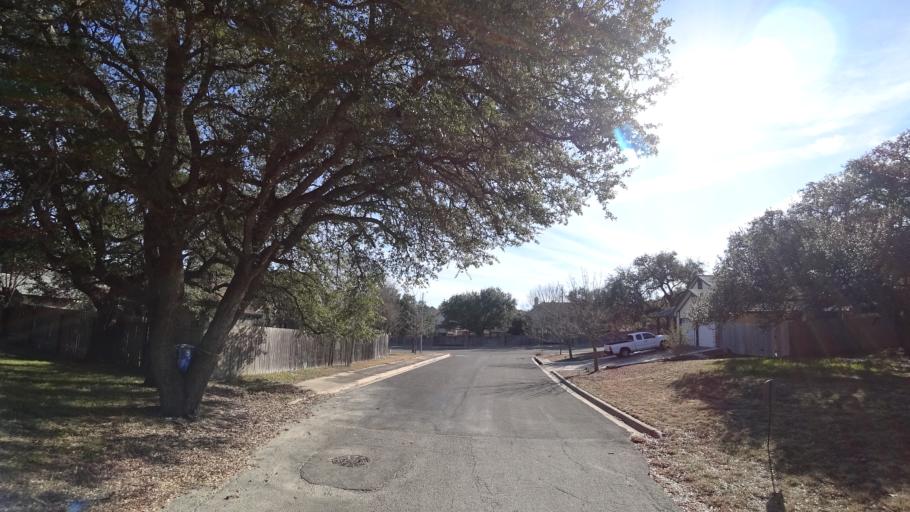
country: US
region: Texas
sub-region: Travis County
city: Wells Branch
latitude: 30.3948
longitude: -97.6972
